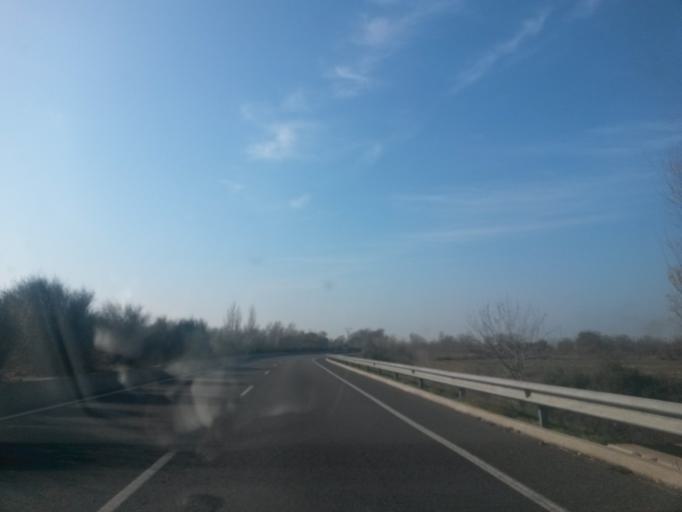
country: ES
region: Catalonia
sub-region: Provincia de Girona
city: Empuriabrava
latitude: 42.2657
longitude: 3.1216
